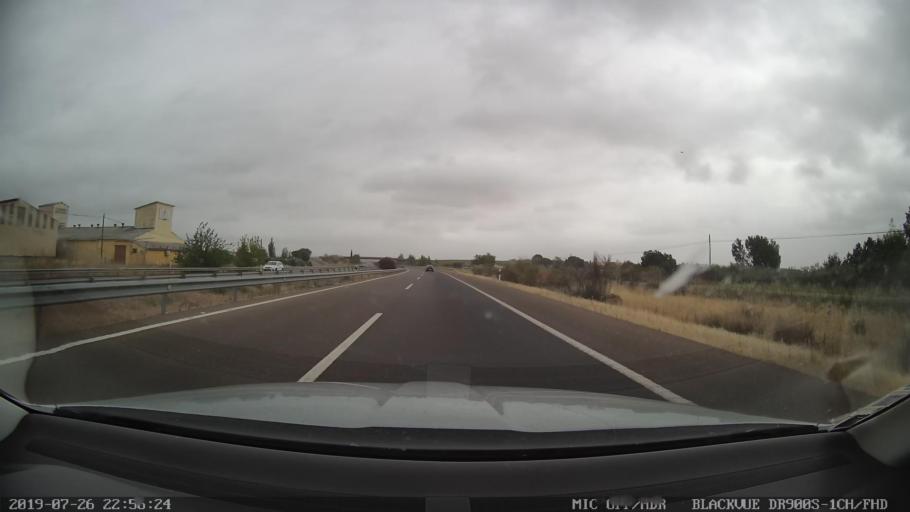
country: ES
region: Extremadura
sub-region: Provincia de Badajoz
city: Calamonte
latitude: 38.8959
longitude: -6.4169
